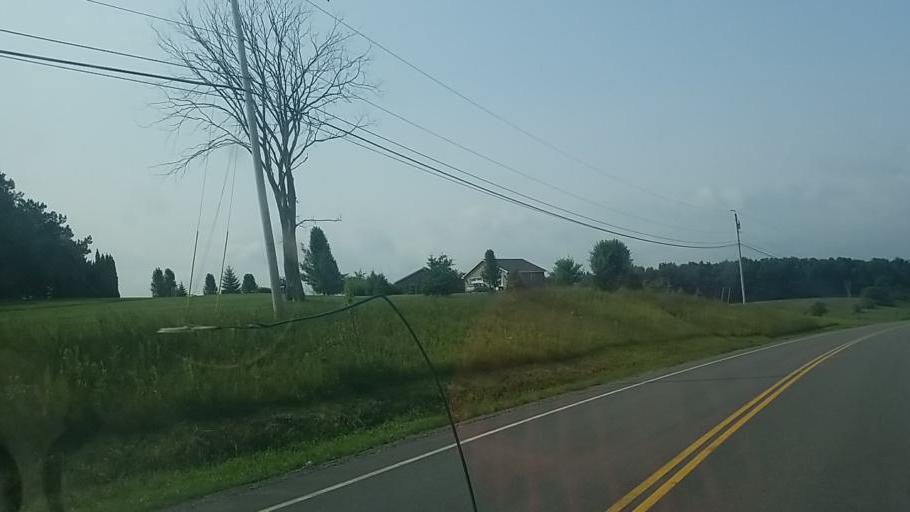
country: US
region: New York
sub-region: Fulton County
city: Johnstown
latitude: 42.9989
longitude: -74.4077
